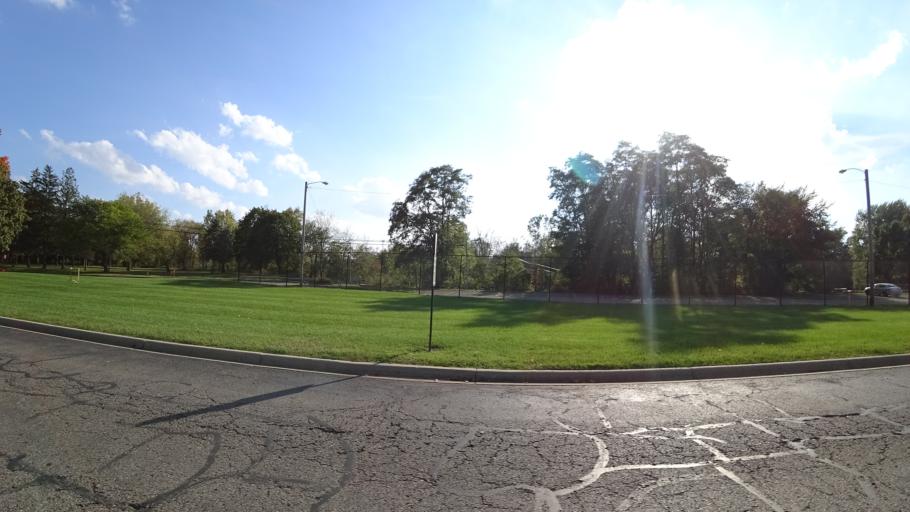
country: US
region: Michigan
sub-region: Saint Joseph County
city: Three Rivers
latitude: 41.9551
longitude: -85.6435
